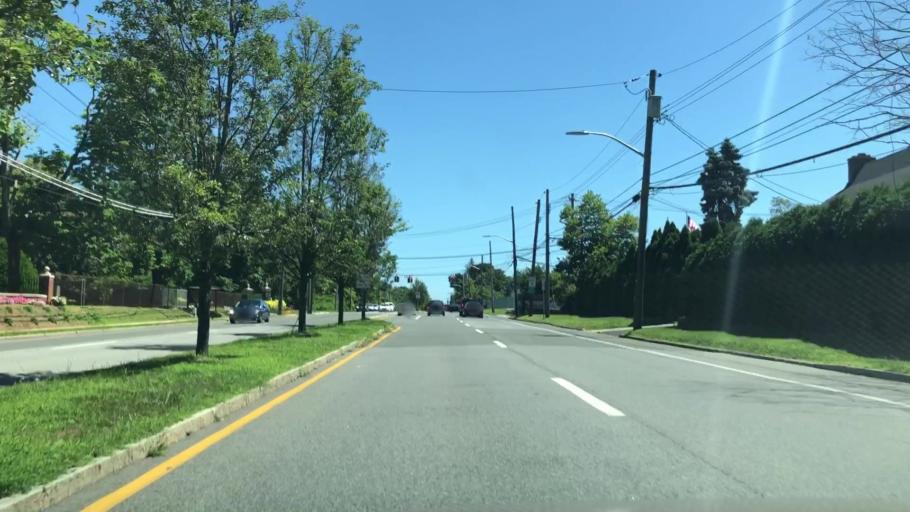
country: US
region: New York
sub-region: Westchester County
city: White Plains
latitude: 41.0147
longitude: -73.7557
